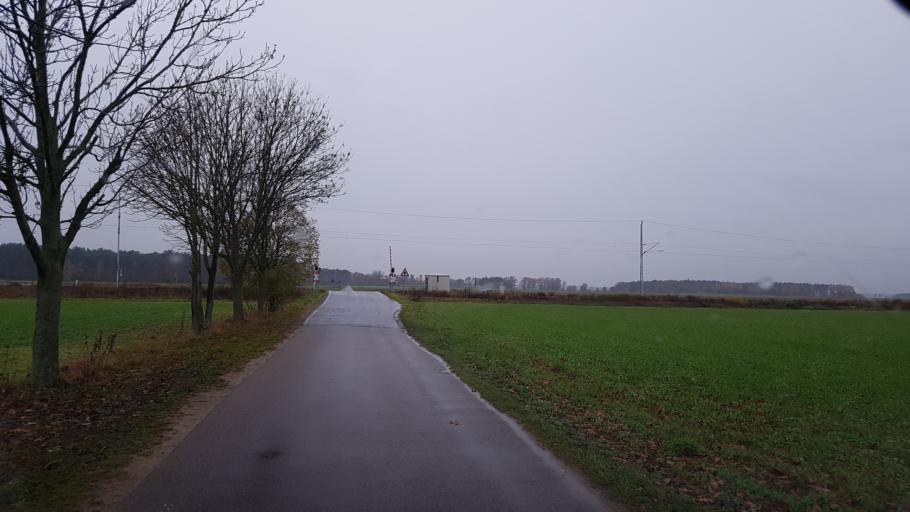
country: DE
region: Brandenburg
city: Herzberg
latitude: 51.6502
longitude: 13.2181
